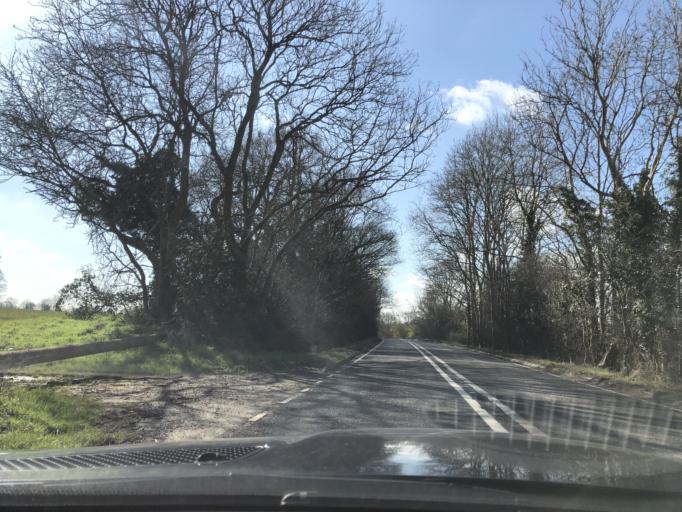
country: GB
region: England
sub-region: Warwickshire
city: Ryton on Dunsmore
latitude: 52.3217
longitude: -1.4214
